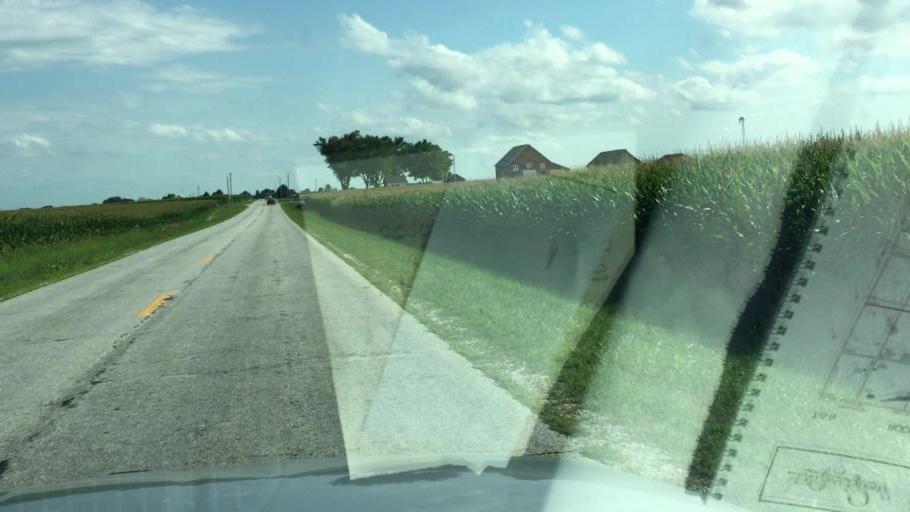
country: US
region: Illinois
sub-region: Hancock County
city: Nauvoo
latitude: 40.5092
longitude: -91.3085
